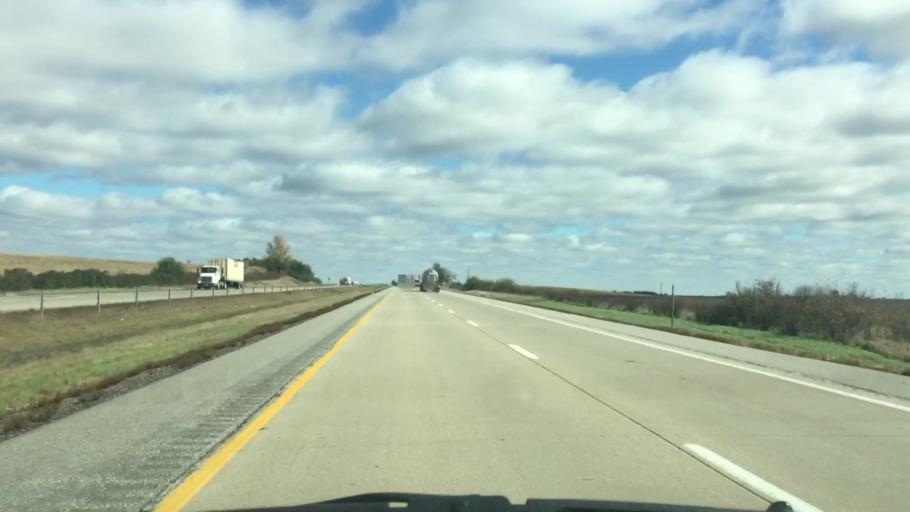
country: US
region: Iowa
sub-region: Poweshiek County
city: Brooklyn
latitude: 41.6948
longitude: -92.4600
